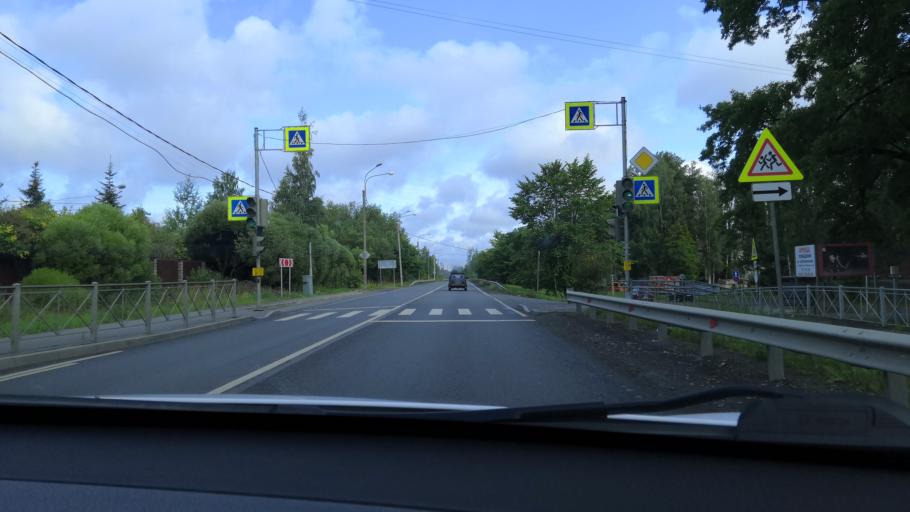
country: RU
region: St.-Petersburg
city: Tyarlevo
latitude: 59.7018
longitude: 30.4402
